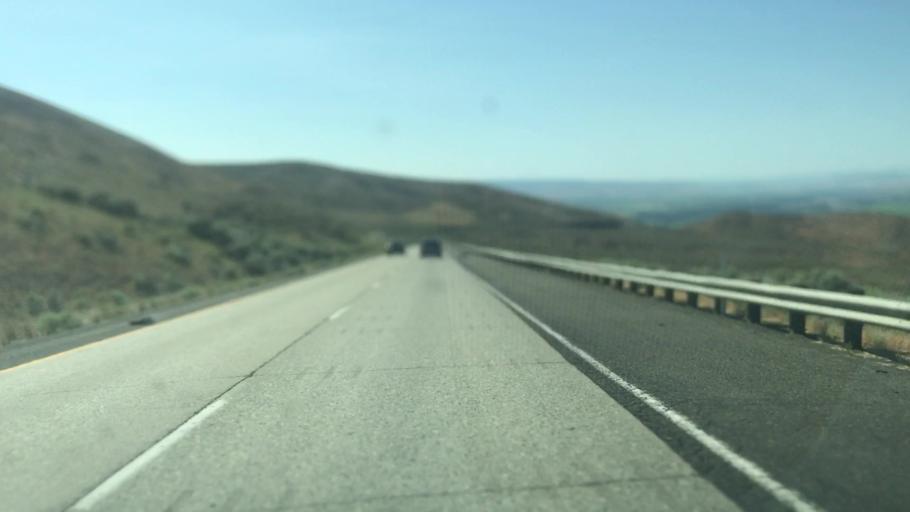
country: US
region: Washington
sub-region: Kittitas County
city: Kittitas
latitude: 46.8918
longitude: -120.4365
